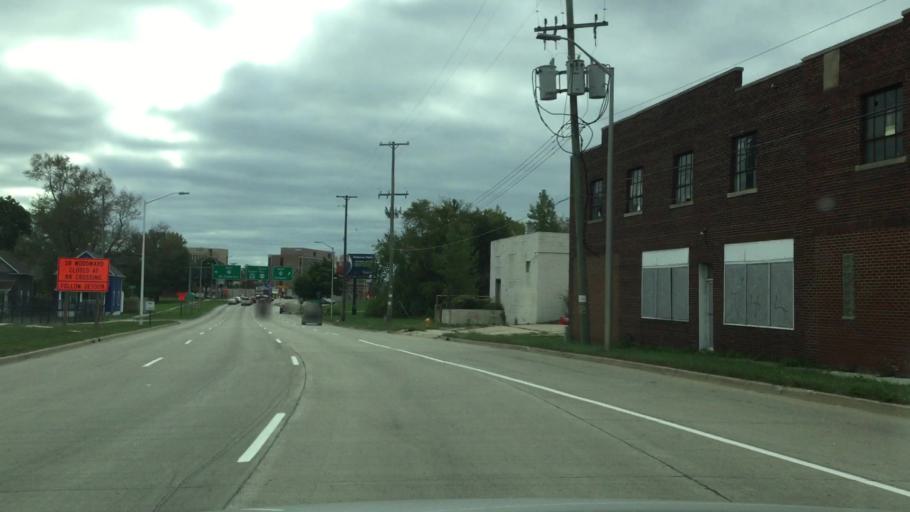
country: US
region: Michigan
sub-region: Oakland County
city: Pontiac
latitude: 42.6402
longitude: -83.2981
